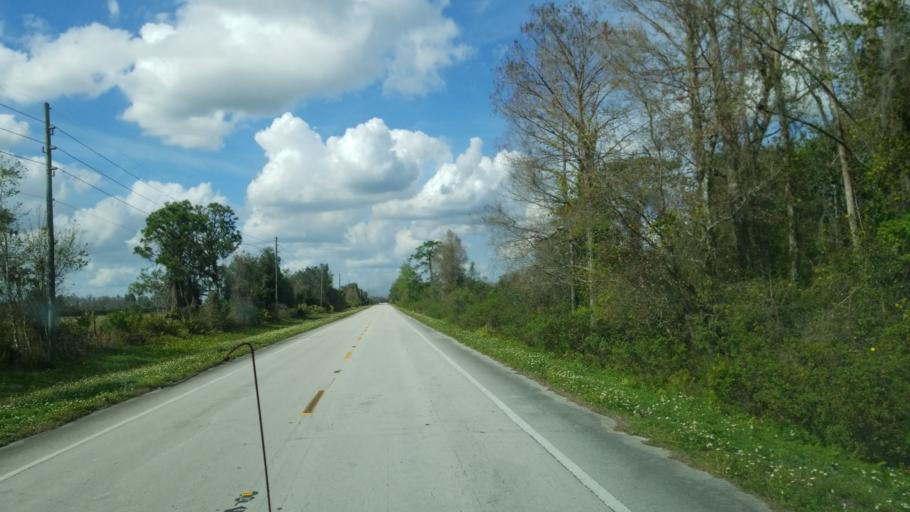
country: US
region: Florida
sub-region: Osceola County
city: Saint Cloud
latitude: 28.0092
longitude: -81.0262
